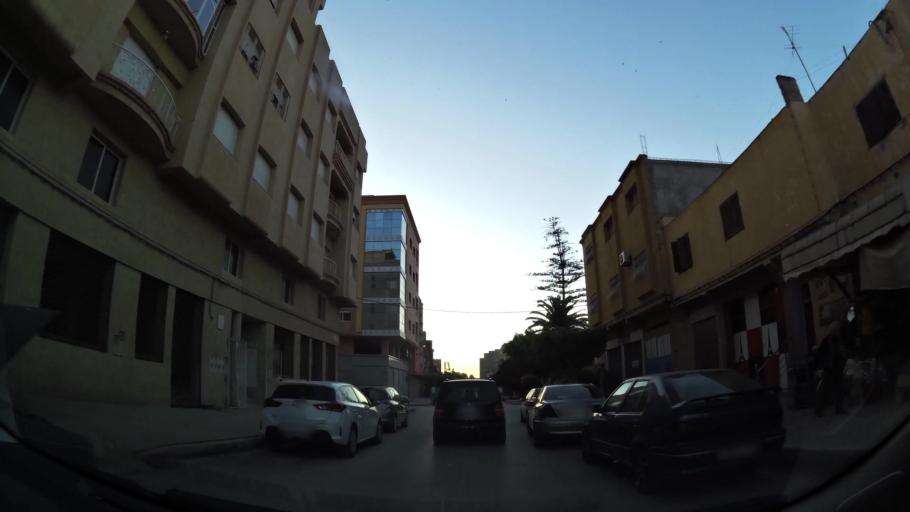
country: MA
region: Oriental
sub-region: Berkane-Taourirt
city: Berkane
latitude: 34.9242
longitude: -2.3316
